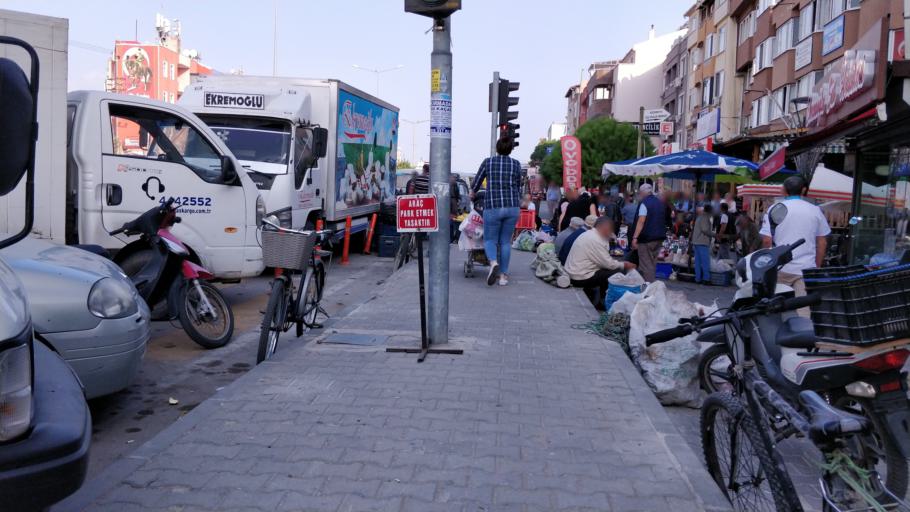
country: TR
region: Canakkale
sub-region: Merkez
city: Kucukkuyu
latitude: 39.5479
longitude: 26.6053
